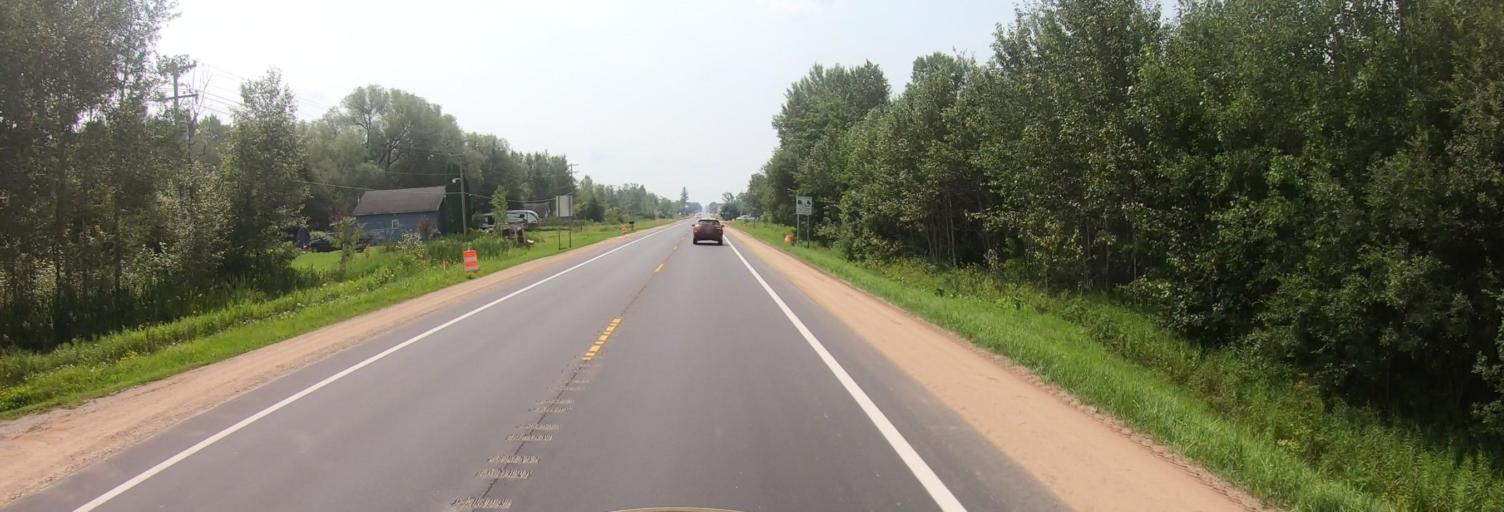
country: US
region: Michigan
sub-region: Luce County
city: Newberry
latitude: 46.3634
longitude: -85.5099
